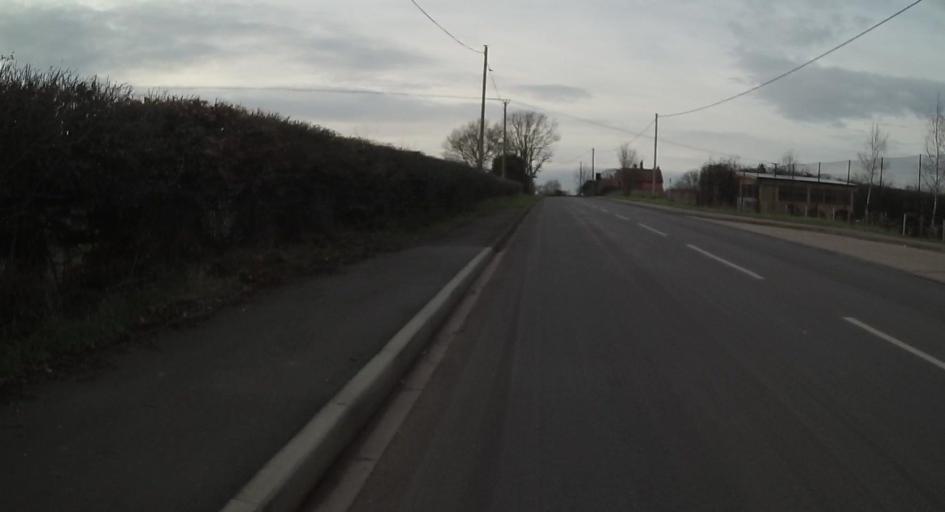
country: GB
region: England
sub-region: West Berkshire
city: Calcot
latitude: 51.4128
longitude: -1.0477
